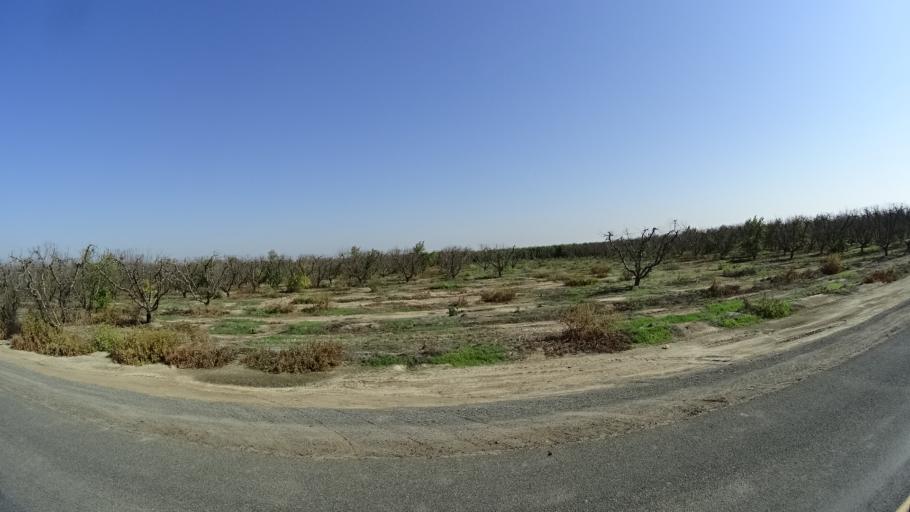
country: US
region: California
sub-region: Kings County
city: Lucerne
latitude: 36.3866
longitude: -119.5789
